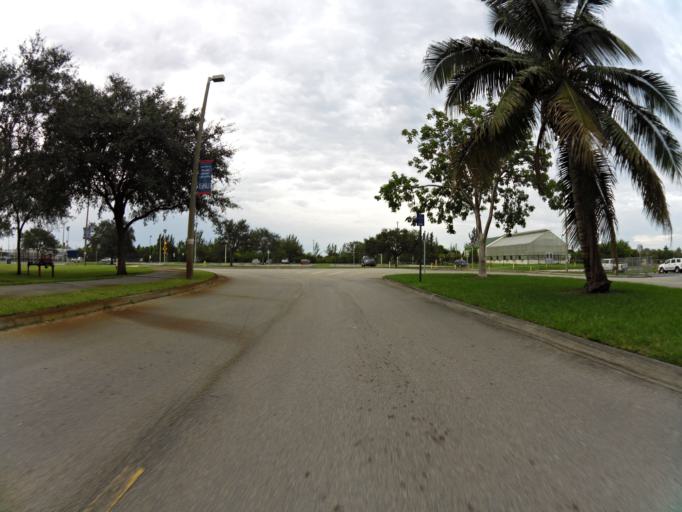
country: US
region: Florida
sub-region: Broward County
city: Davie
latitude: 26.0821
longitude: -80.2336
